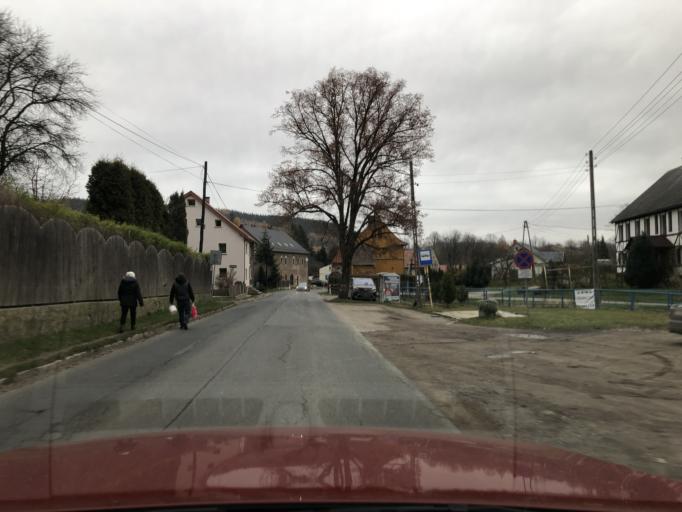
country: PL
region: Lower Silesian Voivodeship
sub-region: Powiat walbrzyski
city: Stare Bogaczowice
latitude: 50.8038
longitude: 16.1956
